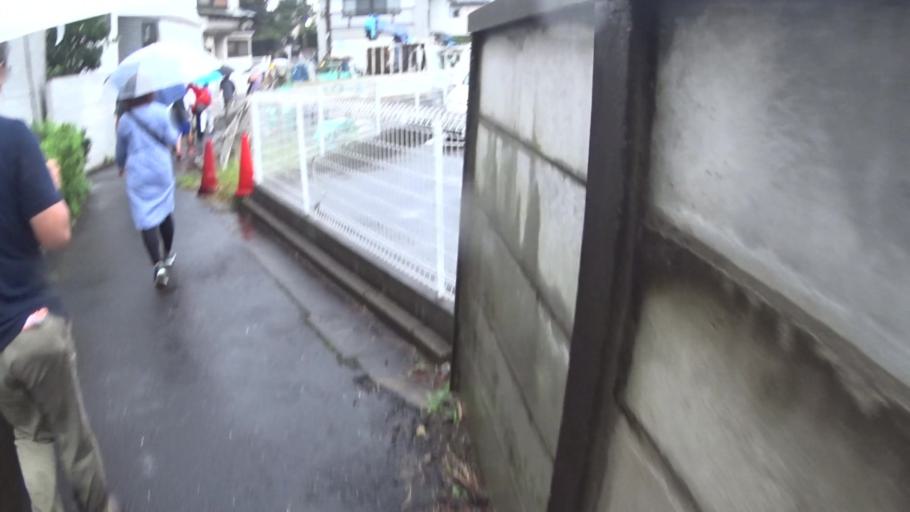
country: JP
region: Saitama
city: Wako
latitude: 35.7399
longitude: 139.6509
